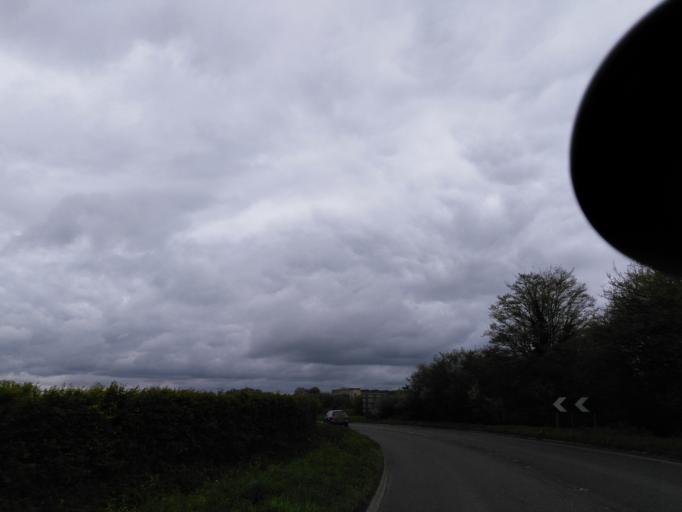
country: GB
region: England
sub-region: Wiltshire
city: Norton
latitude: 51.5358
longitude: -2.1310
